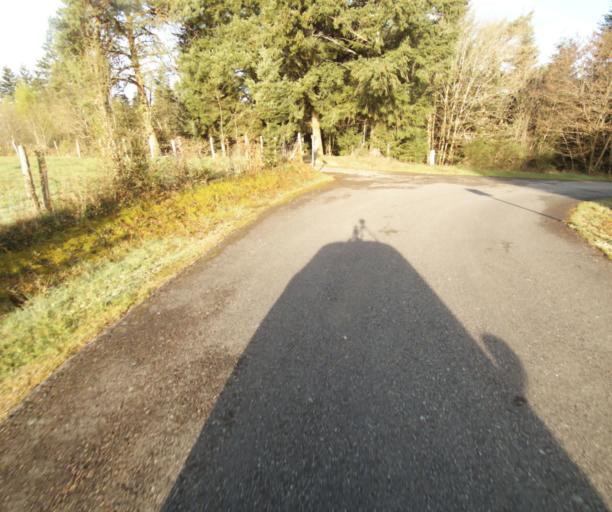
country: FR
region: Limousin
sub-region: Departement de la Correze
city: Naves
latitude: 45.3049
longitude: 1.8320
